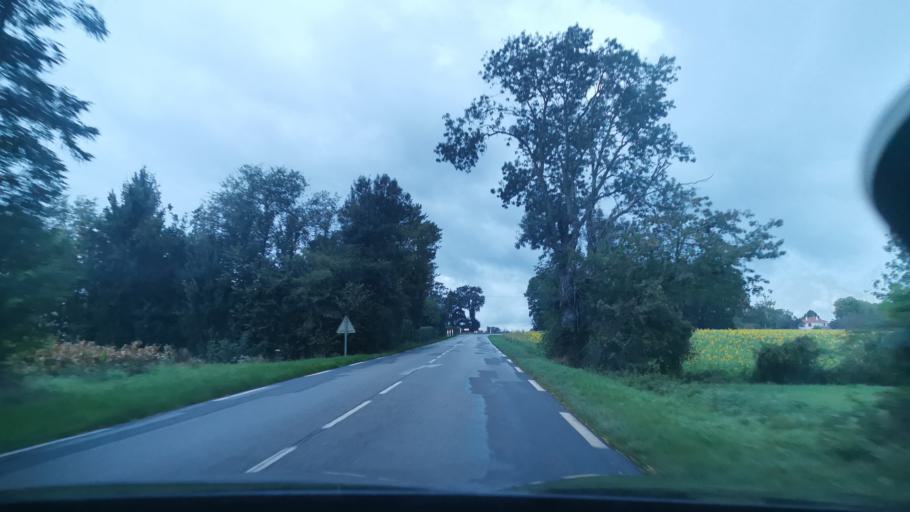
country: FR
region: Rhone-Alpes
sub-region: Departement de l'Ain
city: Vonnas
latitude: 46.2010
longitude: 4.9441
